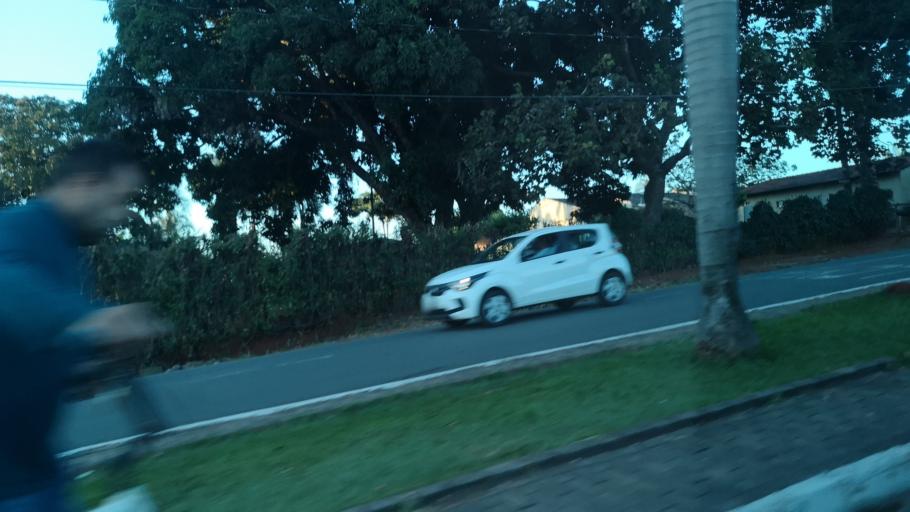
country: BR
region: Goias
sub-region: Senador Canedo
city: Senador Canedo
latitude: -16.6917
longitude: -49.0960
